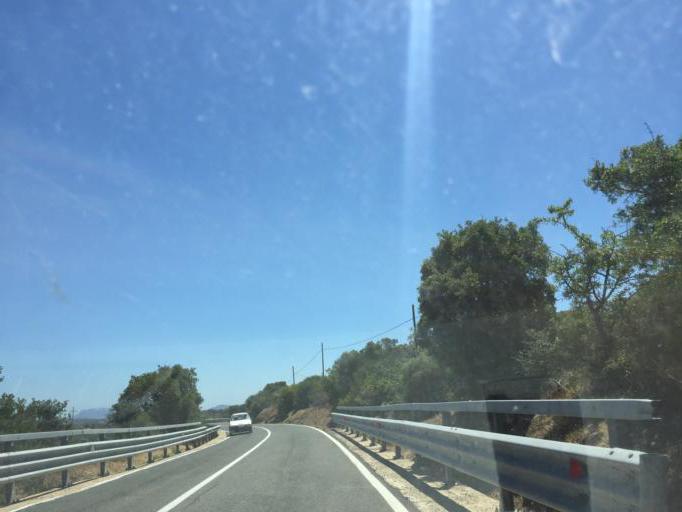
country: IT
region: Sardinia
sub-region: Provincia di Olbia-Tempio
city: Telti
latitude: 40.8919
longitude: 9.3220
